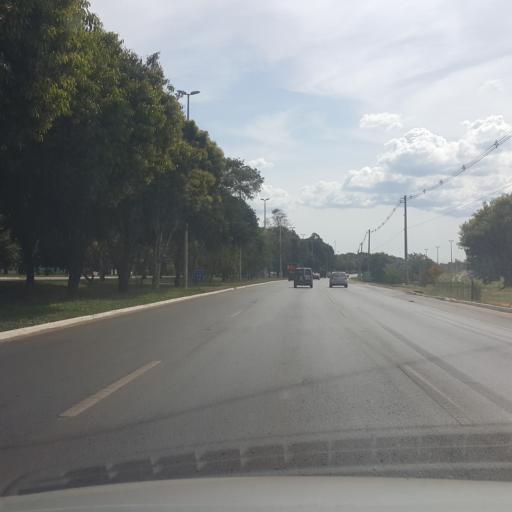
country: BR
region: Federal District
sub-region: Brasilia
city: Brasilia
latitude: -15.8085
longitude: -48.0584
